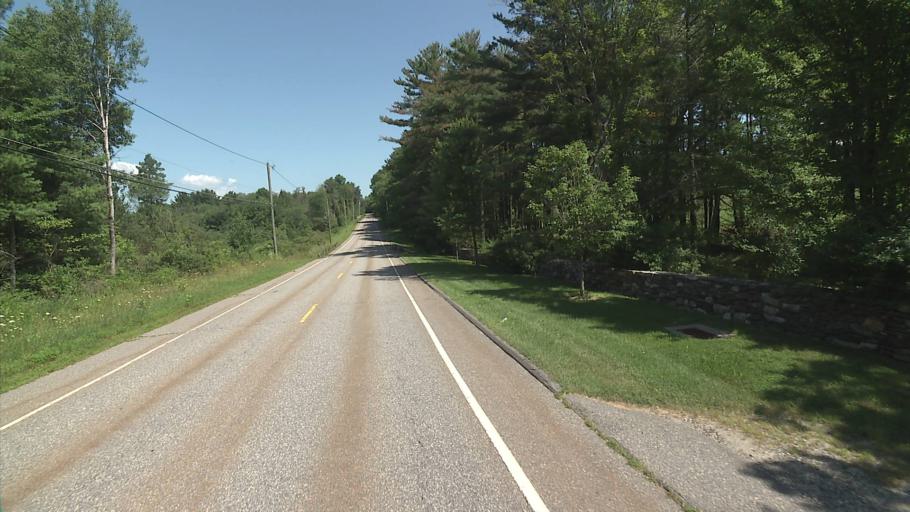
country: US
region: Connecticut
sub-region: Litchfield County
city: New Preston
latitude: 41.7612
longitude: -73.3529
